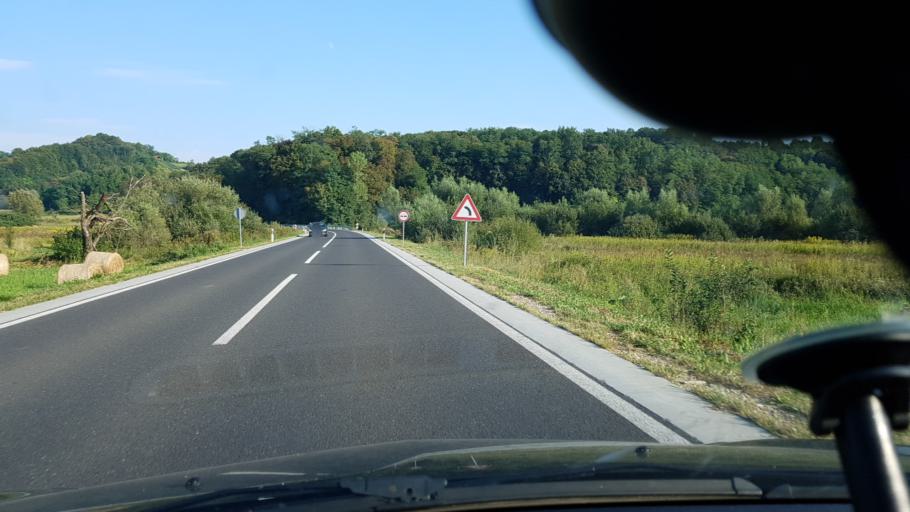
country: HR
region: Krapinsko-Zagorska
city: Zabok
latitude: 46.0313
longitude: 15.8316
